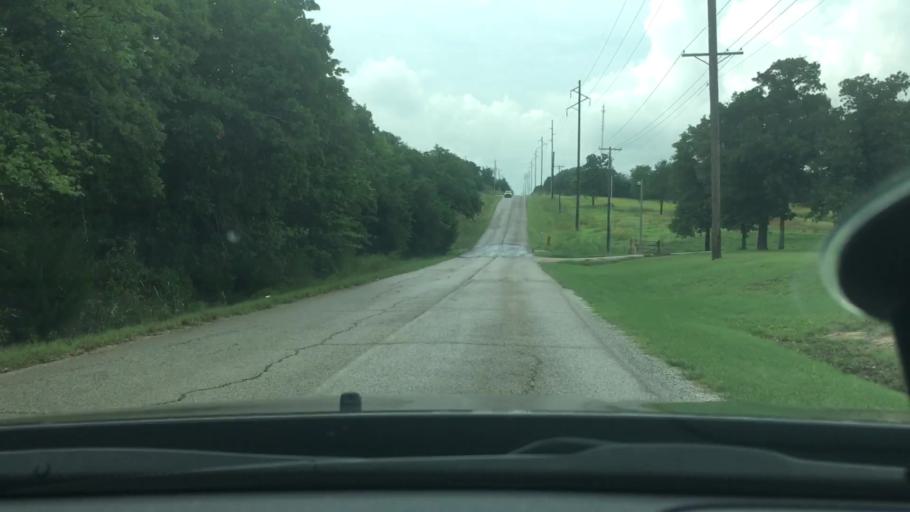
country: US
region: Oklahoma
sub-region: Carter County
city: Healdton
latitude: 34.2191
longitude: -97.4923
